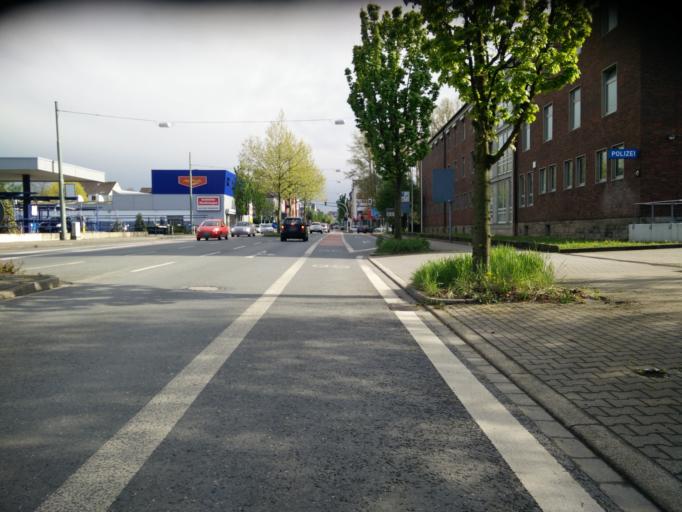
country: DE
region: North Rhine-Westphalia
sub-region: Regierungsbezirk Arnsberg
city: Bochum
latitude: 51.4972
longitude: 7.2121
